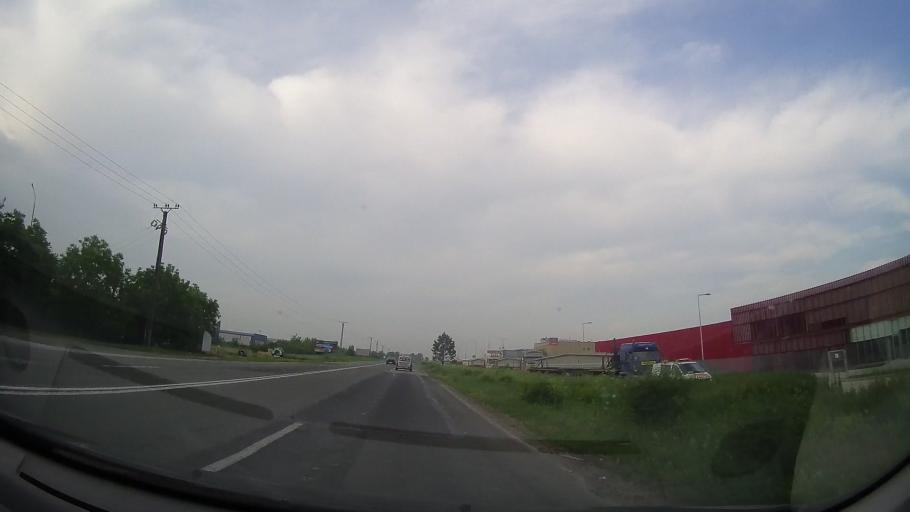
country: RO
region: Timis
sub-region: Comuna Giroc
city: Chisoda
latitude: 45.6969
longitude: 21.1791
